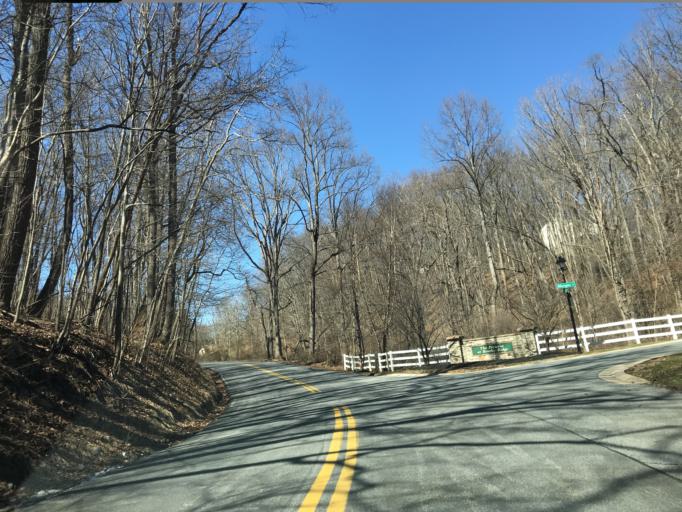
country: US
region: Pennsylvania
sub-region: York County
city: New Freedom
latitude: 39.6758
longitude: -76.6809
